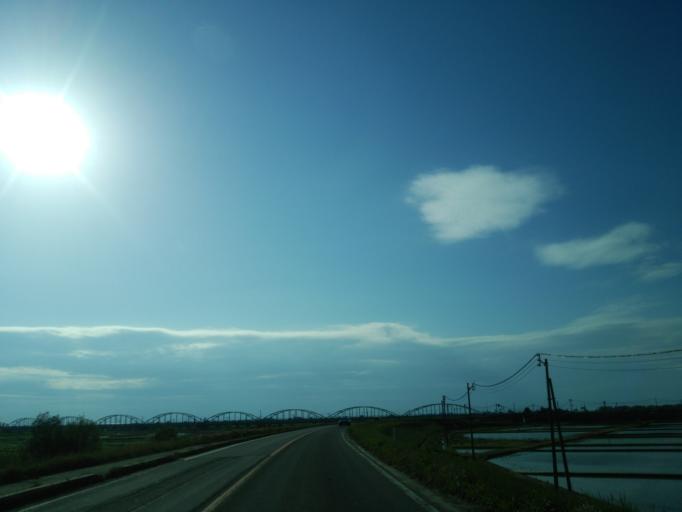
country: JP
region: Niigata
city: Niitsu-honcho
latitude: 37.8104
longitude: 139.1645
